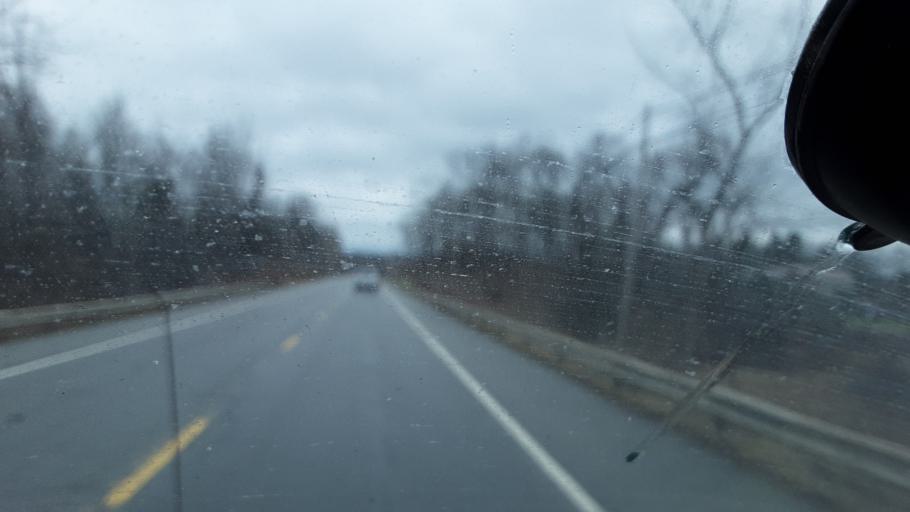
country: US
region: New York
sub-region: Erie County
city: Holland
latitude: 42.5959
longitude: -78.4968
